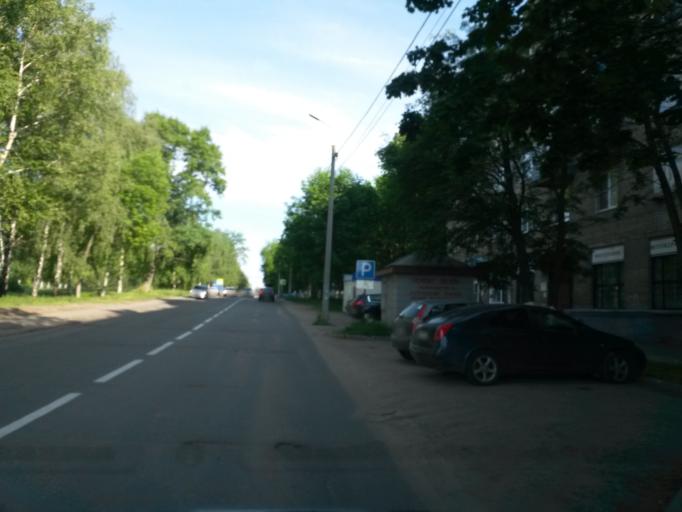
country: RU
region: Jaroslavl
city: Yaroslavl
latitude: 57.5842
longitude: 39.8451
